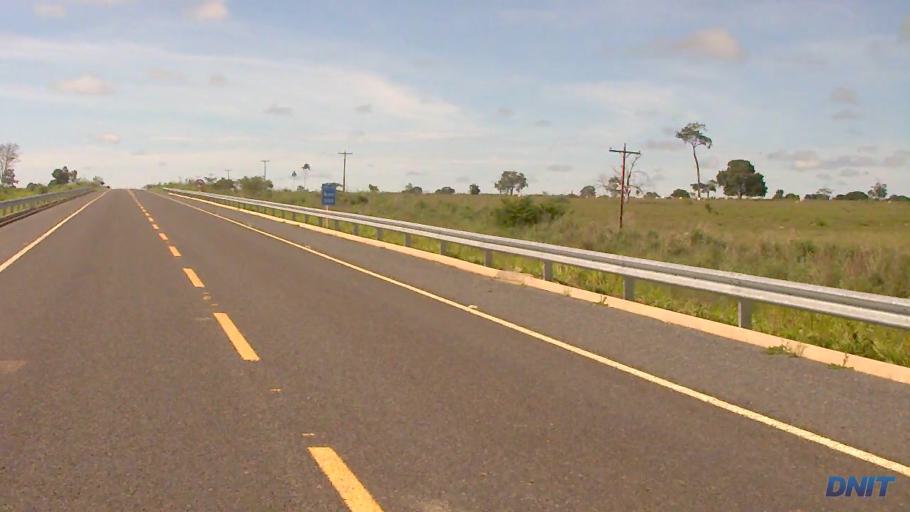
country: BR
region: Goias
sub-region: Sao Miguel Do Araguaia
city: Sao Miguel do Araguaia
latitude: -13.3460
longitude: -50.1507
